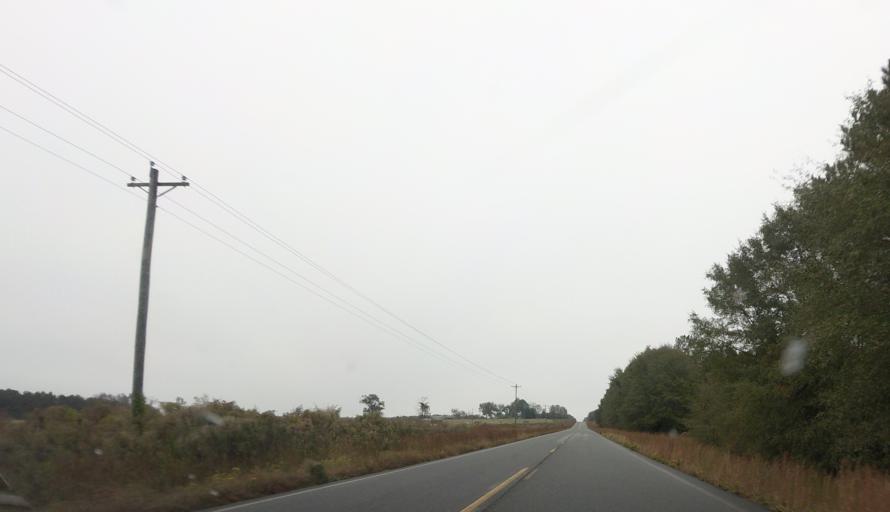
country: US
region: Georgia
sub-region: Marion County
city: Buena Vista
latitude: 32.4003
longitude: -84.4163
